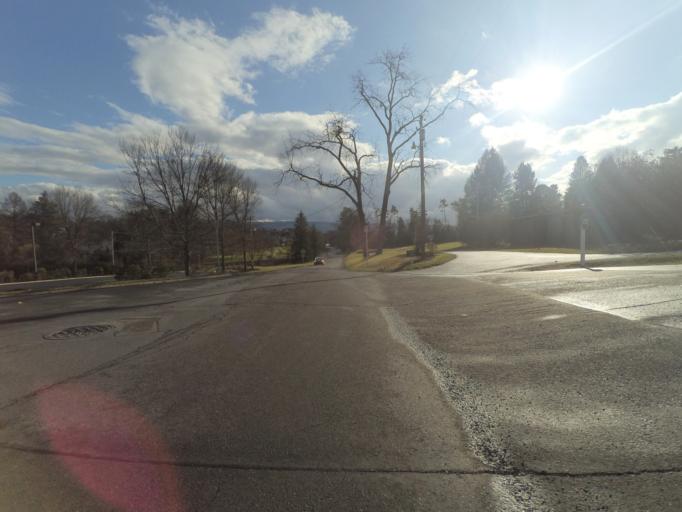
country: US
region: Pennsylvania
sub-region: Centre County
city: Lemont
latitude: 40.7957
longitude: -77.8344
